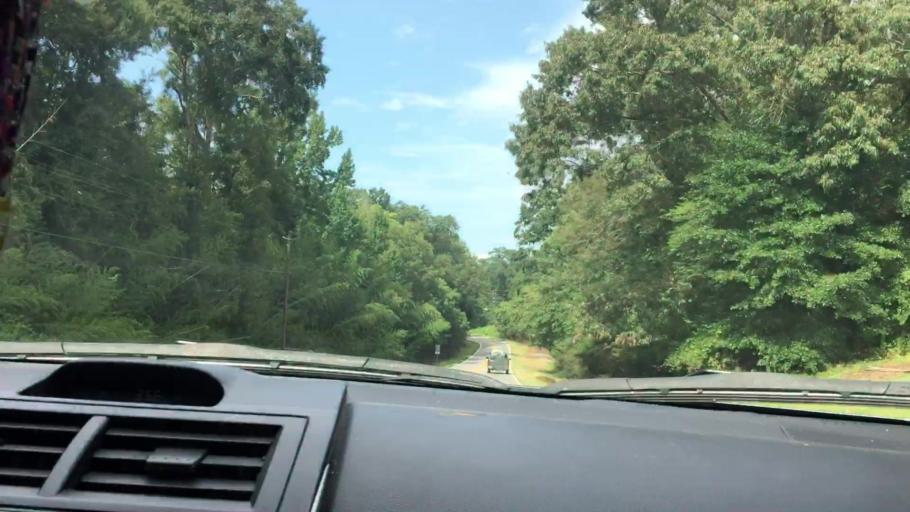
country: US
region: Alabama
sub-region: Hale County
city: Greensboro
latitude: 32.6925
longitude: -87.6072
